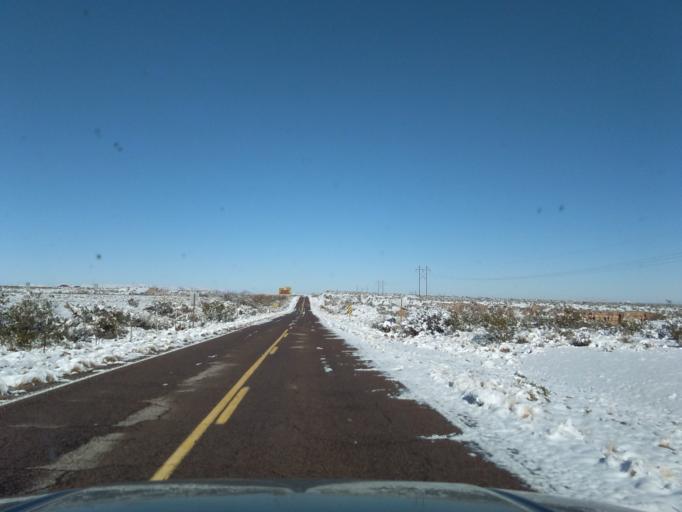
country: US
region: New Mexico
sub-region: Sierra County
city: Elephant Butte
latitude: 33.6299
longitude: -107.1282
